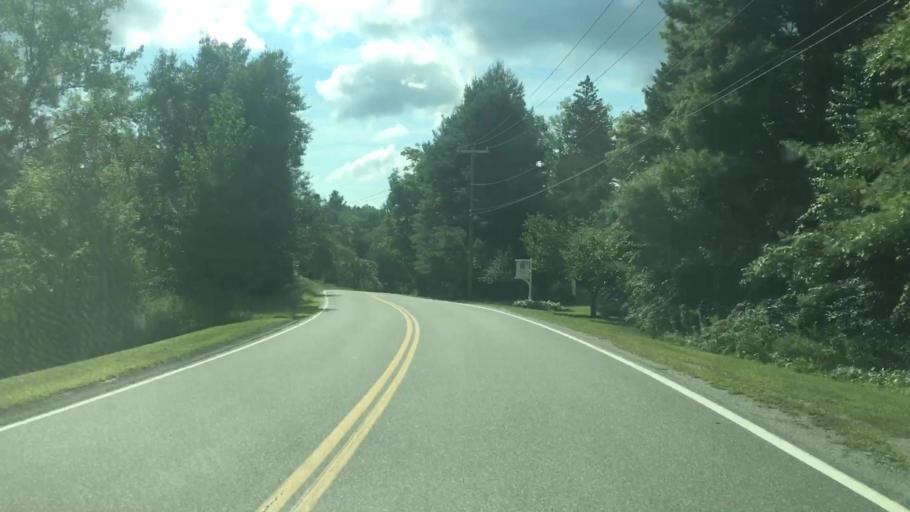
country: US
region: Massachusetts
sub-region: Franklin County
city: Colrain
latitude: 42.6362
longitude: -72.6683
